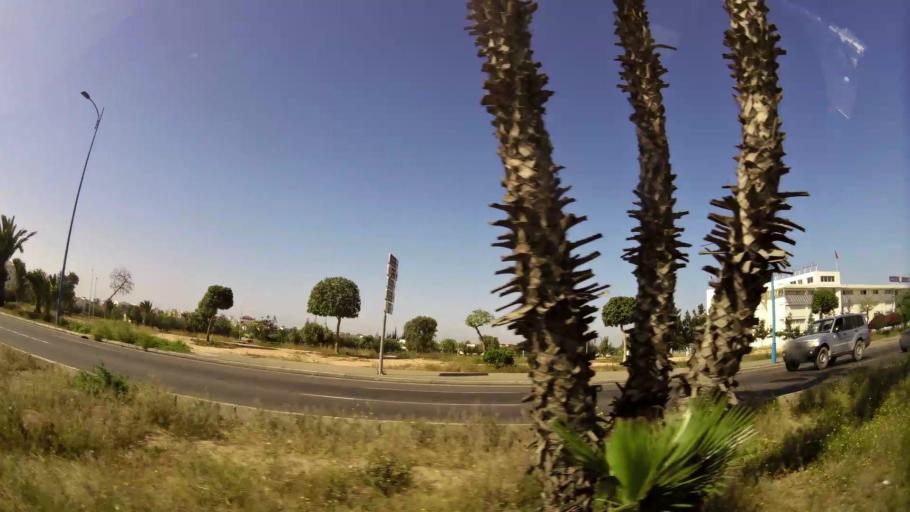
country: MA
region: Oued ed Dahab-Lagouira
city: Dakhla
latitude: 30.4056
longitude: -9.5343
